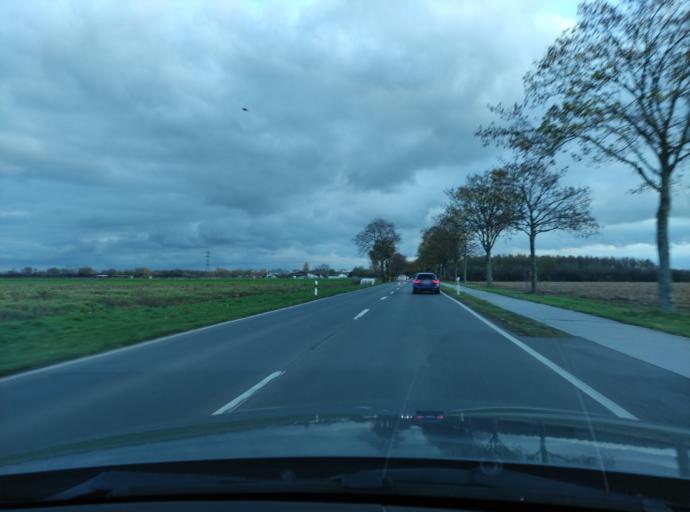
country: DE
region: North Rhine-Westphalia
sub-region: Regierungsbezirk Dusseldorf
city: Dormagen
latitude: 51.1077
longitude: 6.7847
